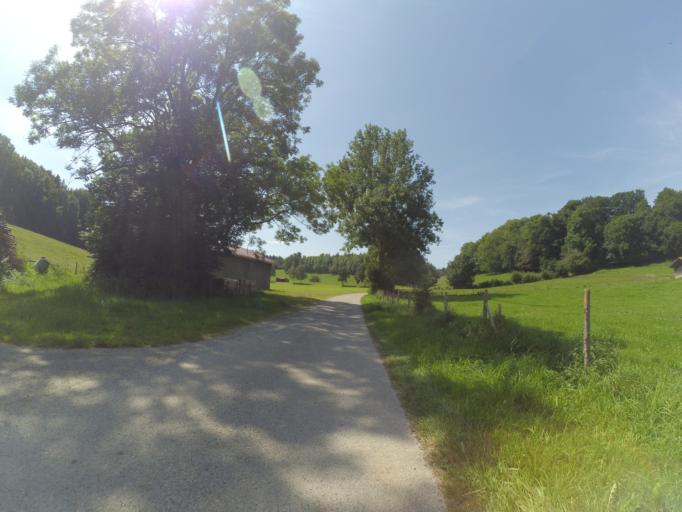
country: DE
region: Bavaria
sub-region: Swabia
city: Baisweil
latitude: 47.9622
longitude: 10.5304
